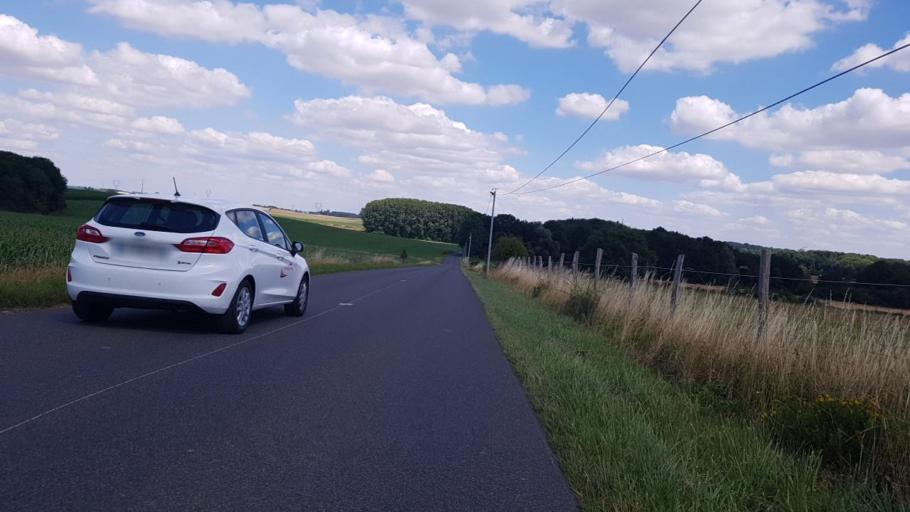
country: FR
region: Ile-de-France
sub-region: Departement de Seine-et-Marne
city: Moussy-le-Neuf
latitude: 49.0709
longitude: 2.6198
